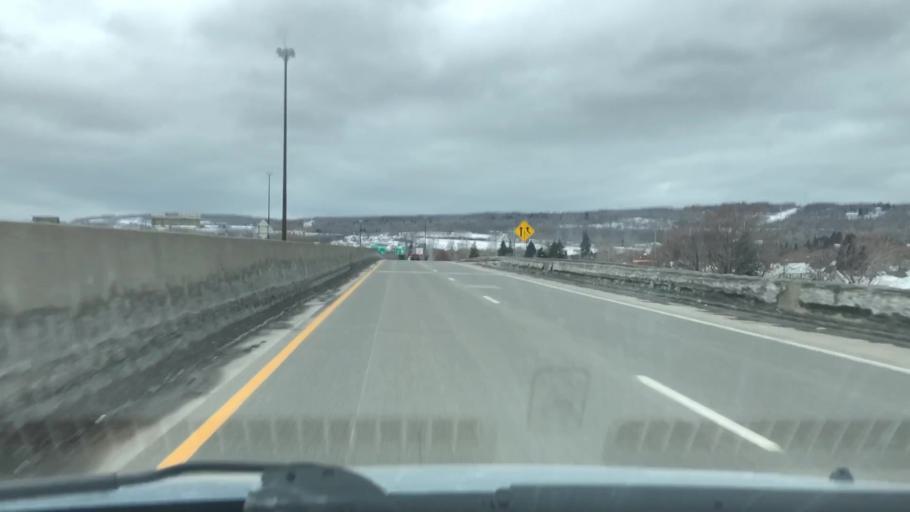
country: US
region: Minnesota
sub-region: Saint Louis County
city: Proctor
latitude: 46.7362
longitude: -92.1689
